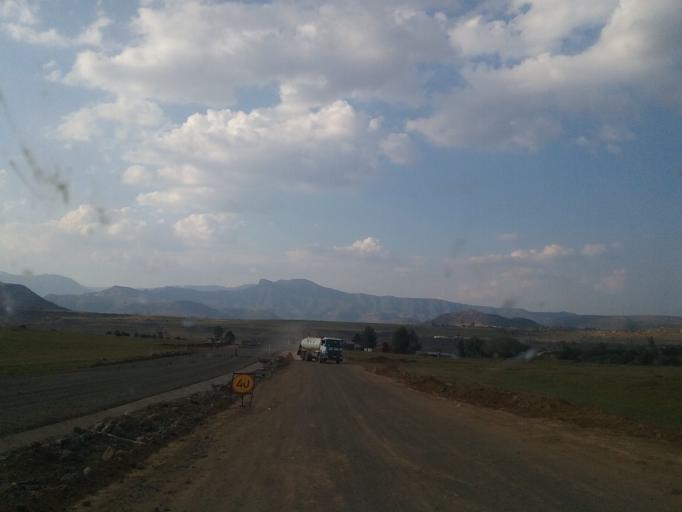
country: LS
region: Quthing
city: Quthing
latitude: -30.4007
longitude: 27.6111
